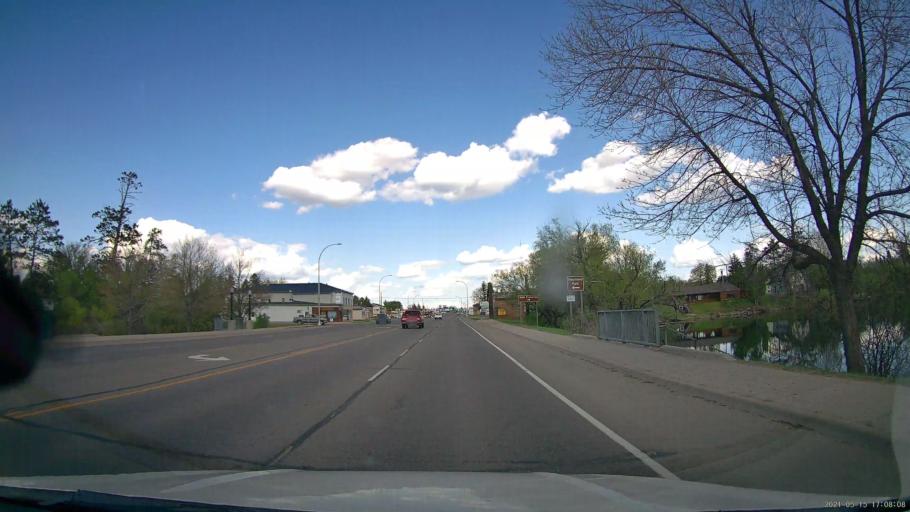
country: US
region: Minnesota
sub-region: Hubbard County
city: Park Rapids
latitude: 46.9221
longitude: -95.0530
